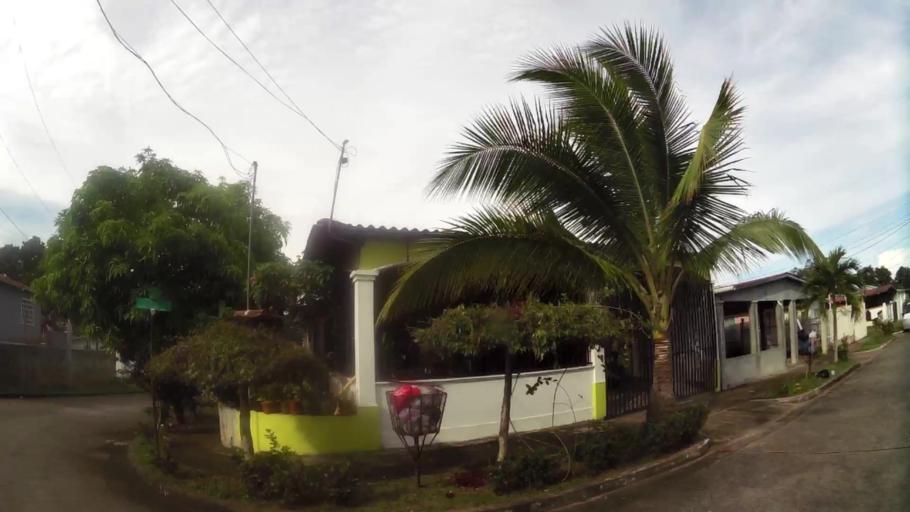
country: PA
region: Panama
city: La Chorrera
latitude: 8.8830
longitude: -79.7656
